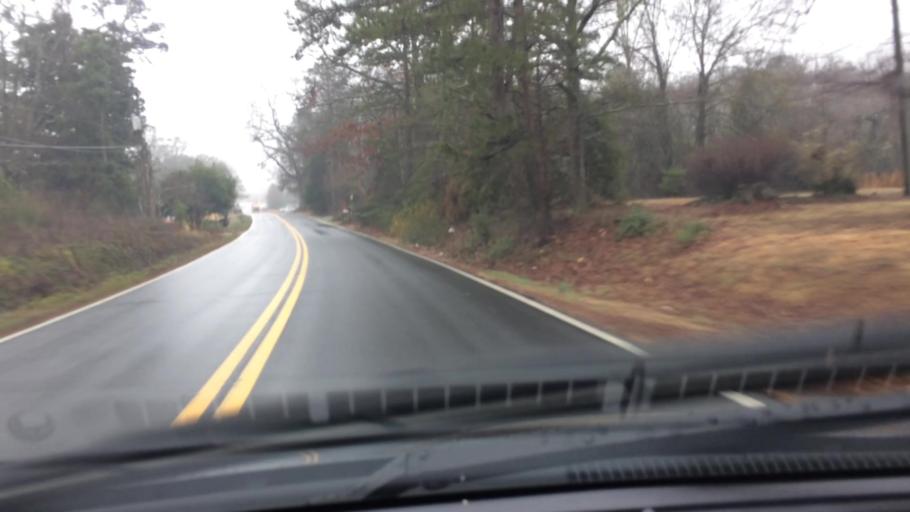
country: US
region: South Carolina
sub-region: Anderson County
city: Williamston
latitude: 34.6374
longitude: -82.4809
